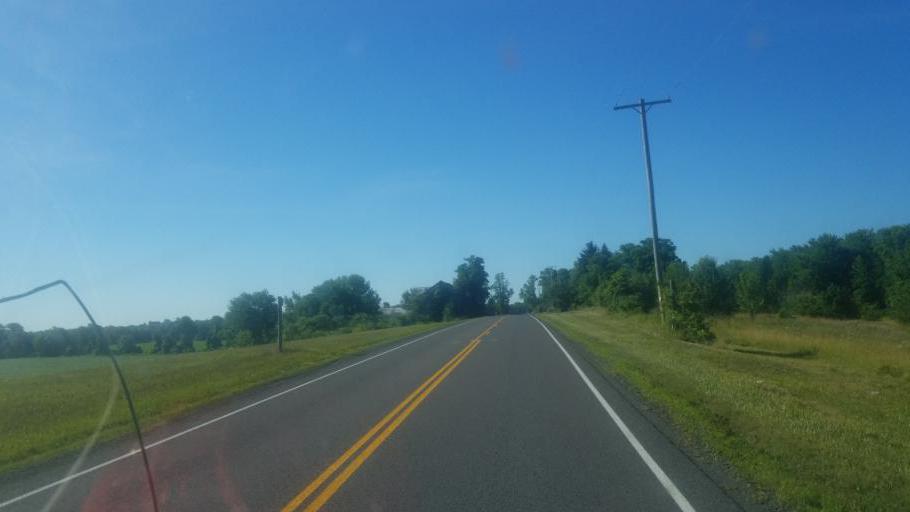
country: US
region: New York
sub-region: Ontario County
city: Phelps
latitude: 42.9061
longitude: -77.0588
